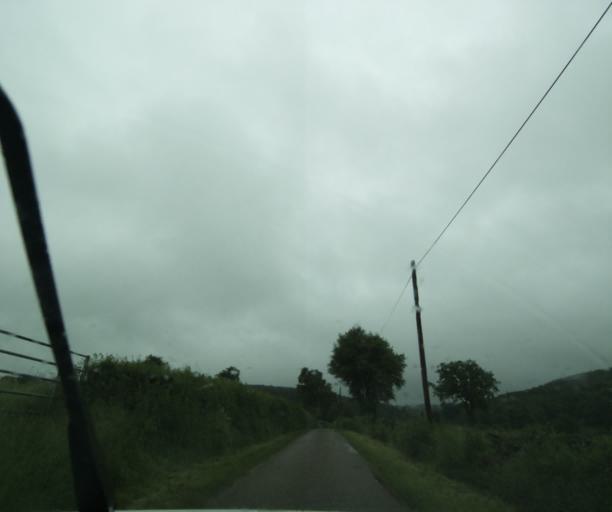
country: FR
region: Bourgogne
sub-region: Departement de Saone-et-Loire
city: Charolles
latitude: 46.3972
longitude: 4.2709
